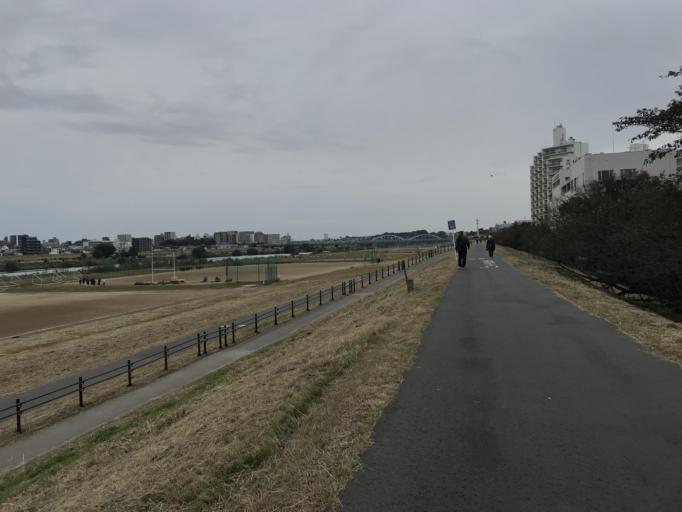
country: JP
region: Kanagawa
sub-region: Kawasaki-shi
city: Kawasaki
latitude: 35.5727
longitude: 139.6760
